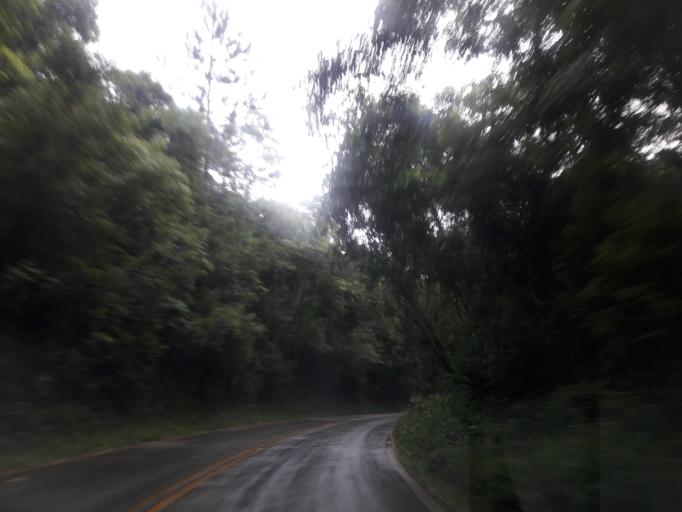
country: BR
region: Sao Paulo
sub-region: Bom Jesus Dos Perdoes
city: Bom Jesus dos Perdoes
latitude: -23.2810
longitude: -46.4227
